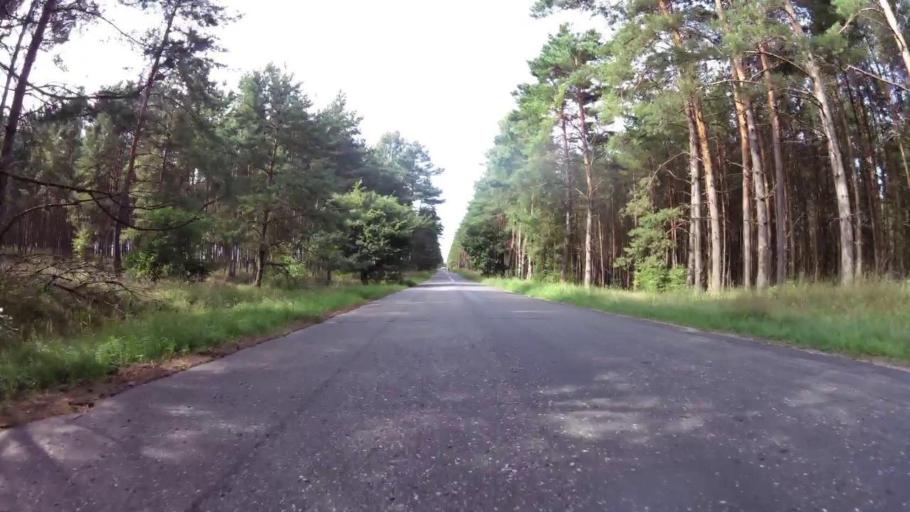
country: PL
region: West Pomeranian Voivodeship
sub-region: Powiat stargardzki
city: Insko
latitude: 53.3871
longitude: 15.5960
